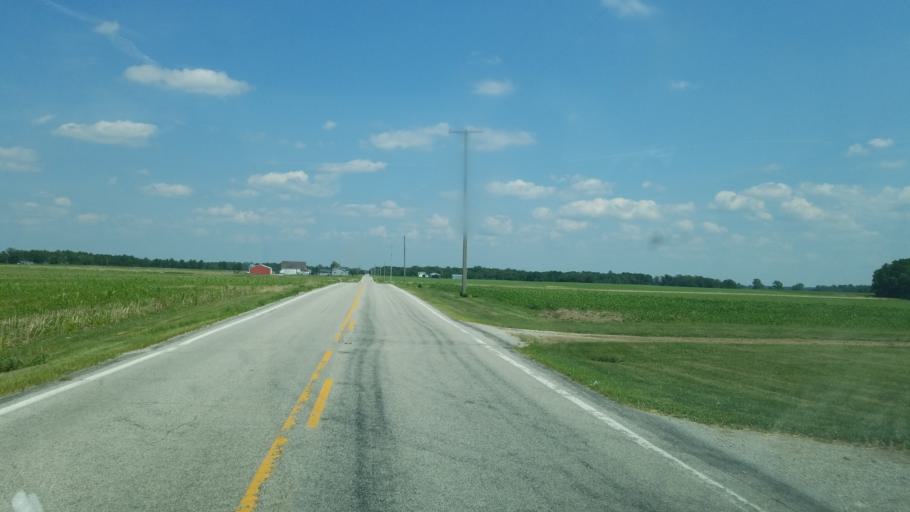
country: US
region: Ohio
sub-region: Huron County
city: Willard
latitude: 41.1256
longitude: -82.8268
